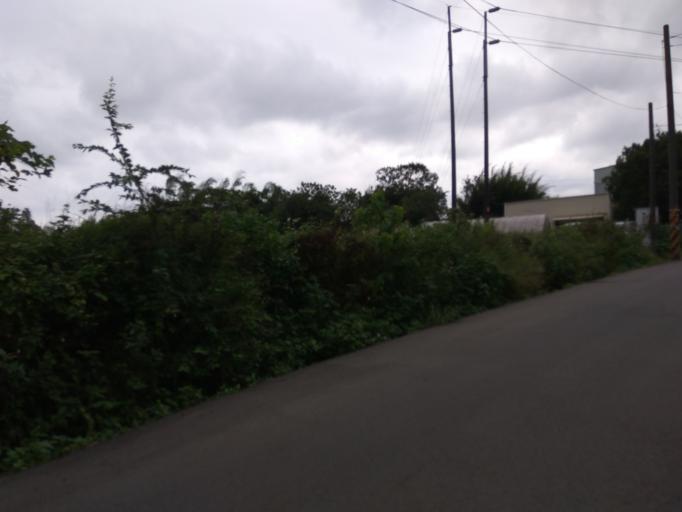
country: TW
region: Taiwan
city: Taoyuan City
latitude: 24.9840
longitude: 121.2287
